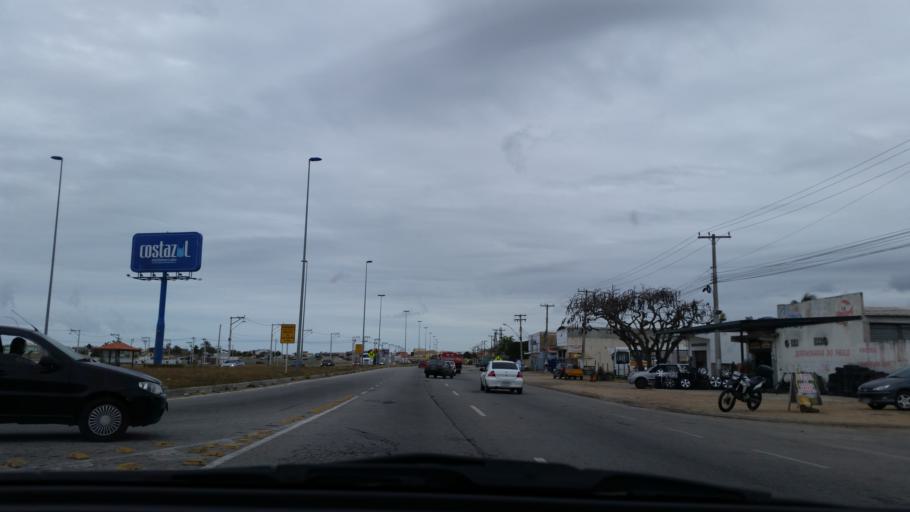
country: BR
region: Rio de Janeiro
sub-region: Sao Pedro Da Aldeia
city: Sao Pedro da Aldeia
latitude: -22.8310
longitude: -42.0921
